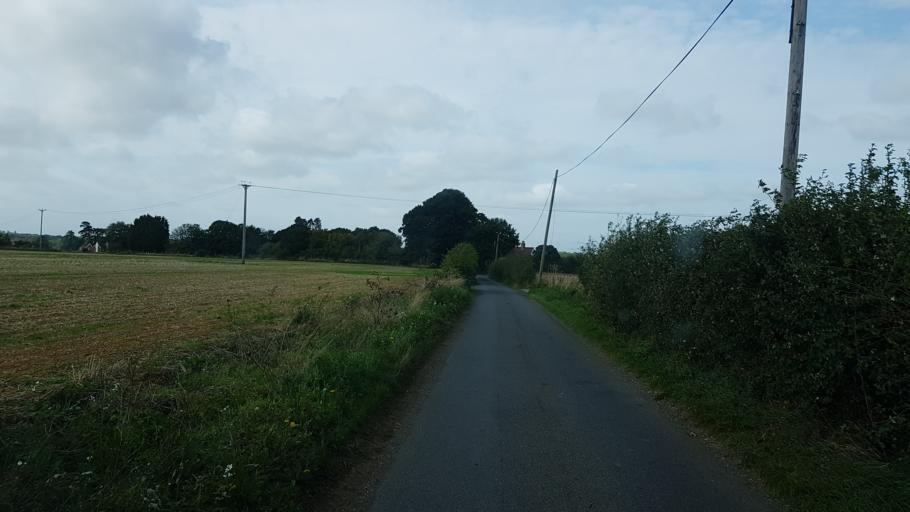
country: GB
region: England
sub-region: Kent
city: Harrietsham
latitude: 51.2382
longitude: 0.6043
